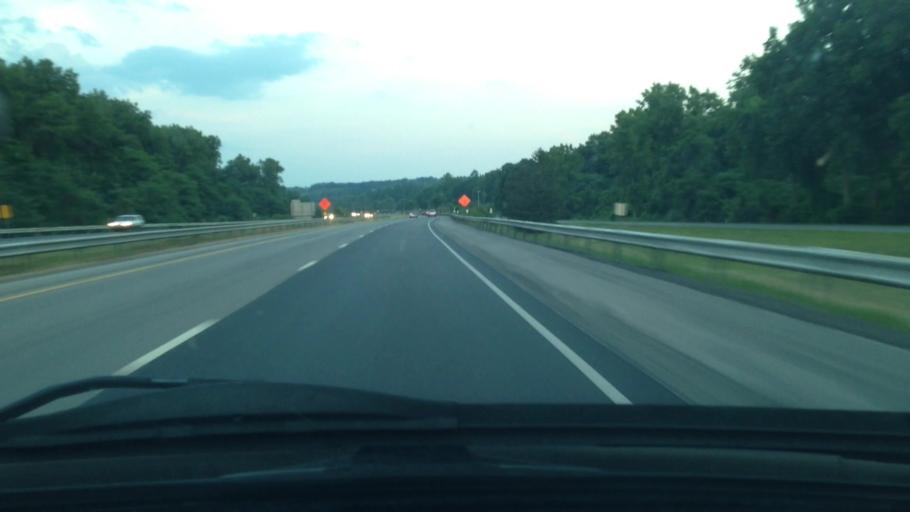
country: US
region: New York
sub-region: Montgomery County
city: Canajoharie
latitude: 42.9013
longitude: -74.5463
